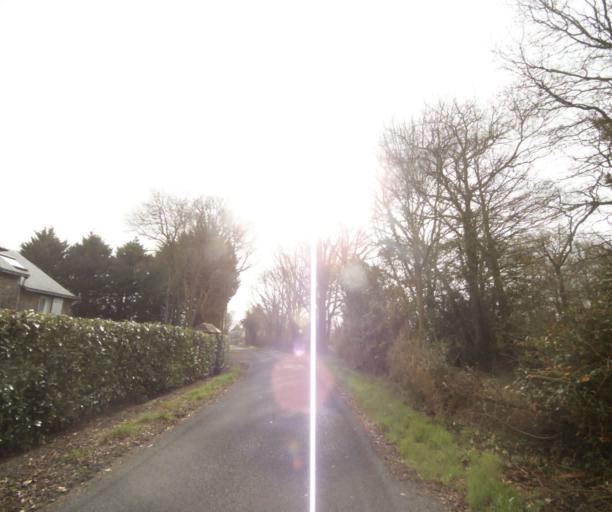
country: FR
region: Pays de la Loire
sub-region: Departement de la Loire-Atlantique
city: Bouvron
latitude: 47.4015
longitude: -1.8835
